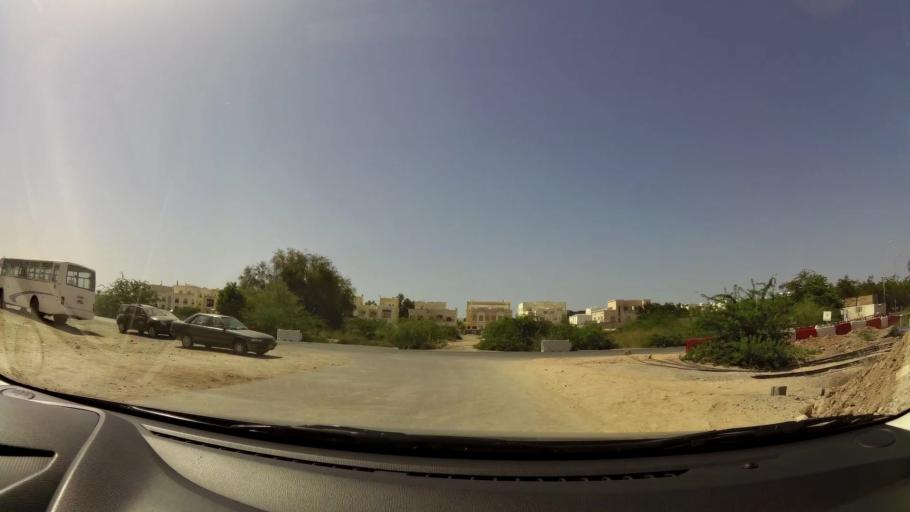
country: OM
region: Muhafazat Masqat
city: Bawshar
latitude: 23.5944
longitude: 58.3500
